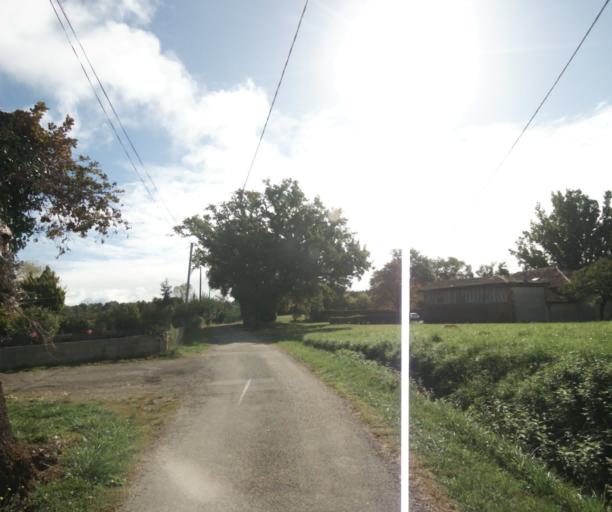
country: FR
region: Midi-Pyrenees
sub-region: Departement du Gers
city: Cazaubon
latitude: 43.8481
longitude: -0.0659
